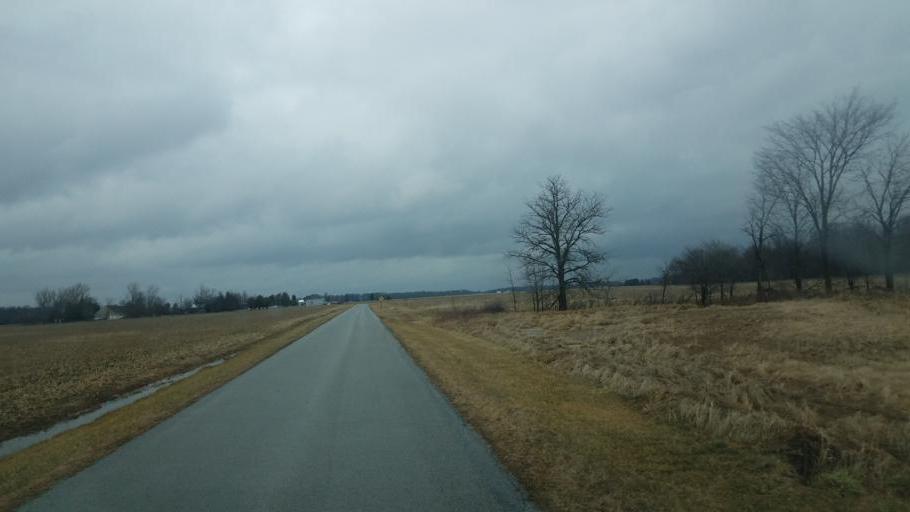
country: US
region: Ohio
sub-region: Hardin County
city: Kenton
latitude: 40.6909
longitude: -83.5592
